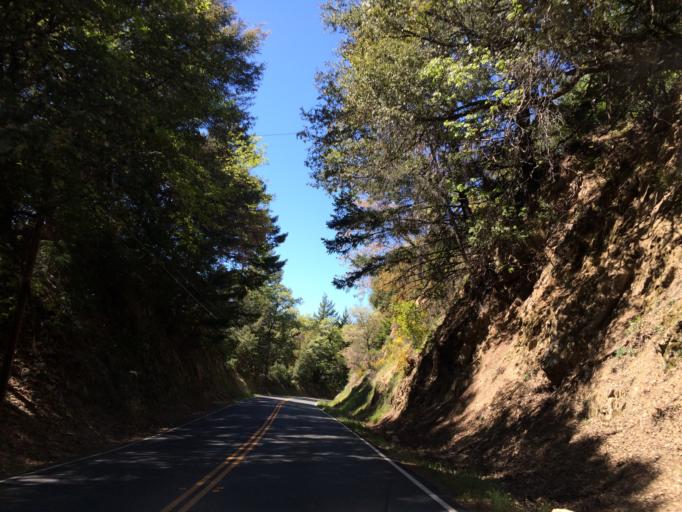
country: US
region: California
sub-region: Santa Clara County
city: Saratoga
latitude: 37.2167
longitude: -122.0702
